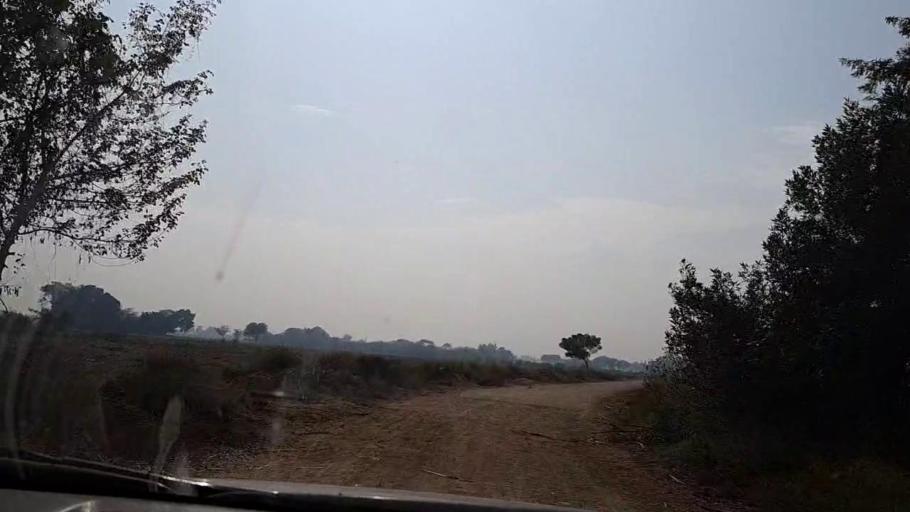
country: PK
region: Sindh
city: Daulatpur
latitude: 26.5357
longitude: 67.9867
